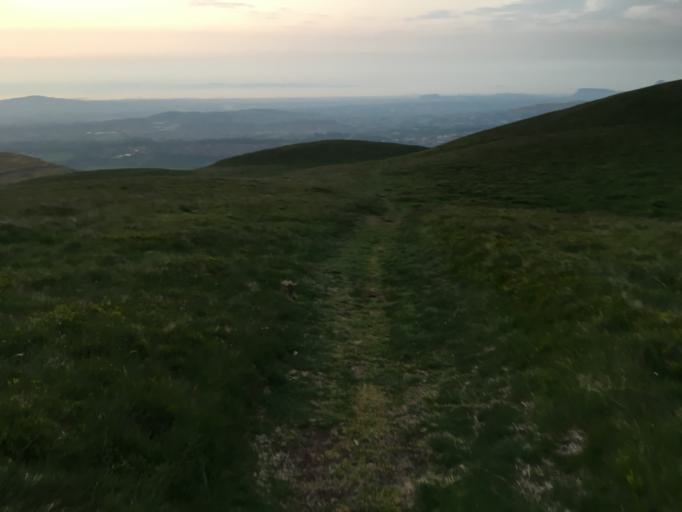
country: GB
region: Scotland
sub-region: Edinburgh
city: Colinton
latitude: 55.8874
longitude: -3.2256
